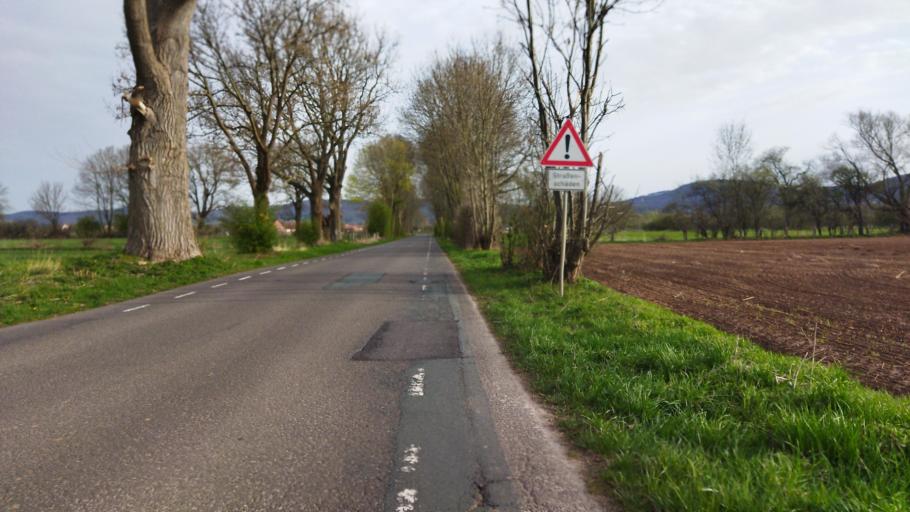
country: DE
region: Lower Saxony
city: Rinteln
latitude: 52.1874
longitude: 9.0269
